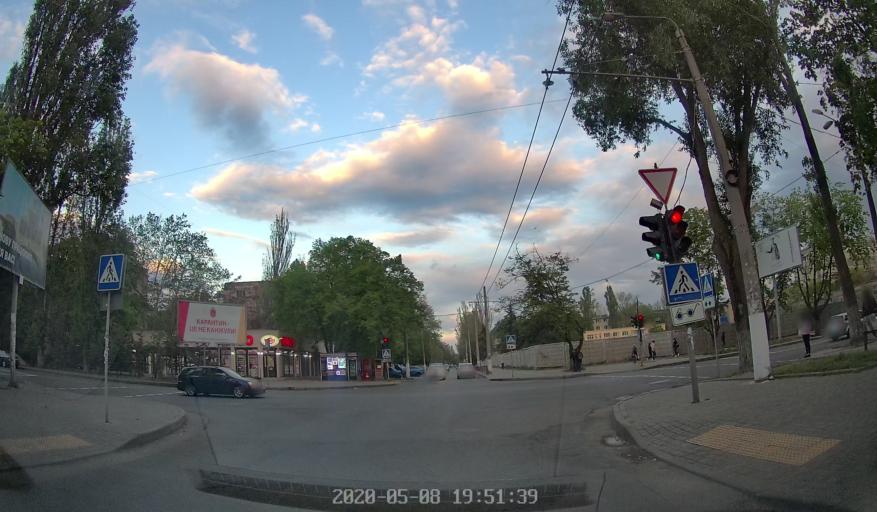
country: NE
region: Zinder
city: Mirriah
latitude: 13.9306
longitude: 9.2127
